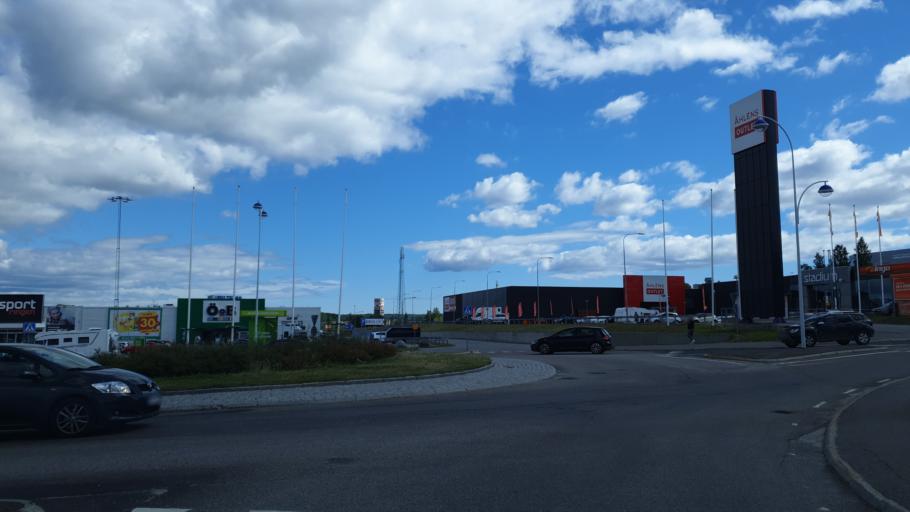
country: SE
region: Vaesternorrland
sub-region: Sundsvalls Kommun
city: Sundsbruk
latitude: 62.4431
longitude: 17.3315
